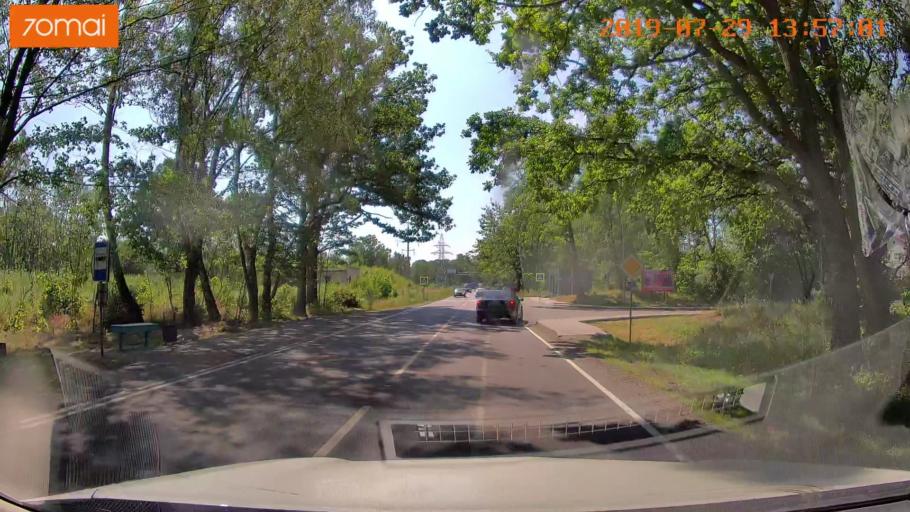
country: RU
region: Kaliningrad
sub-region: Gorod Kaliningrad
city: Baltiysk
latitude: 54.7046
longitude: 19.9452
